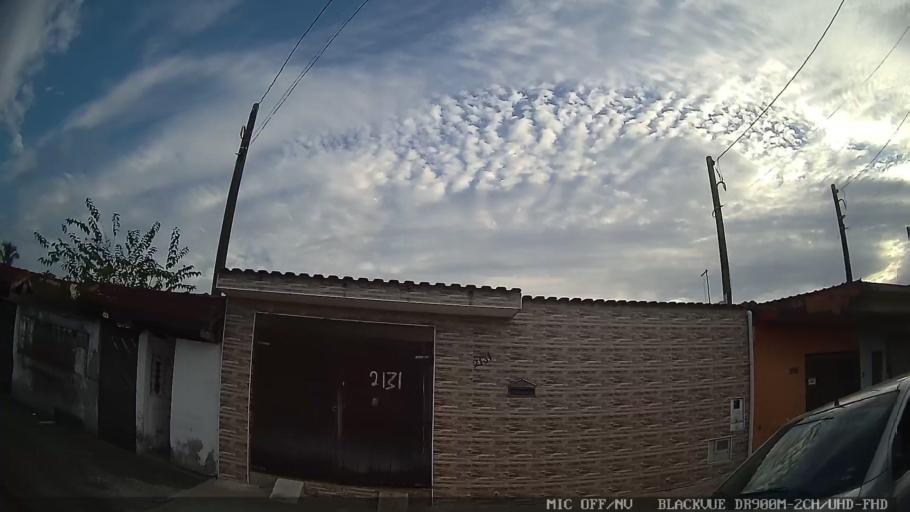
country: BR
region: Sao Paulo
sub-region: Itanhaem
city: Itanhaem
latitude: -24.1612
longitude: -46.7809
